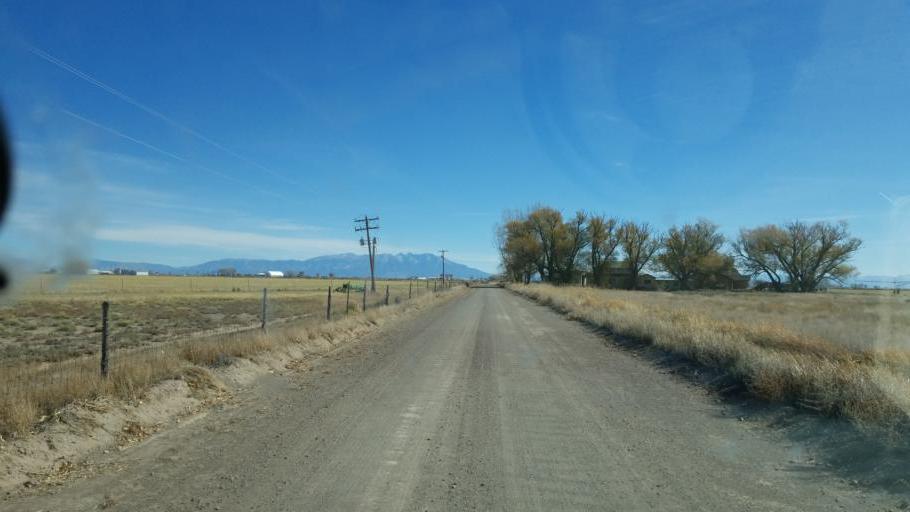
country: US
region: Colorado
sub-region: Rio Grande County
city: Monte Vista
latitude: 37.5313
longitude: -106.0555
